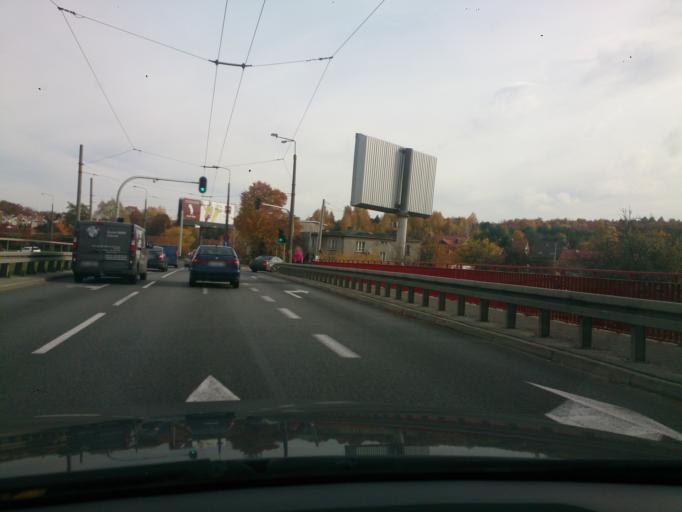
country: PL
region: Pomeranian Voivodeship
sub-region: Gdynia
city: Wielki Kack
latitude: 54.4688
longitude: 18.5082
